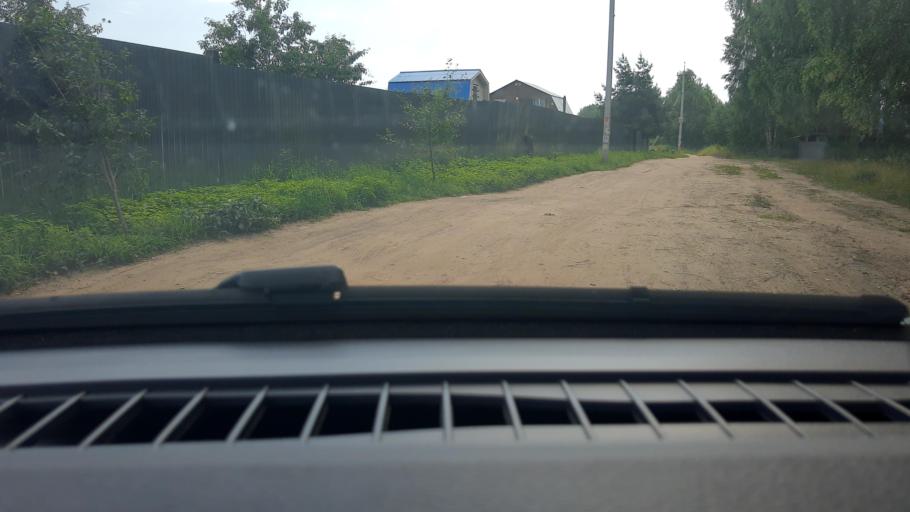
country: RU
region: Nizjnij Novgorod
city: Neklyudovo
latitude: 56.4283
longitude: 43.9993
